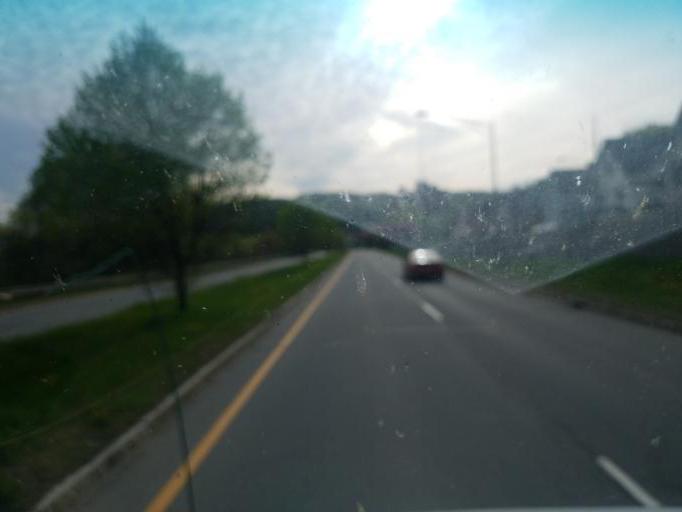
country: US
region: New York
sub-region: Herkimer County
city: Little Falls
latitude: 43.0426
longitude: -74.8535
